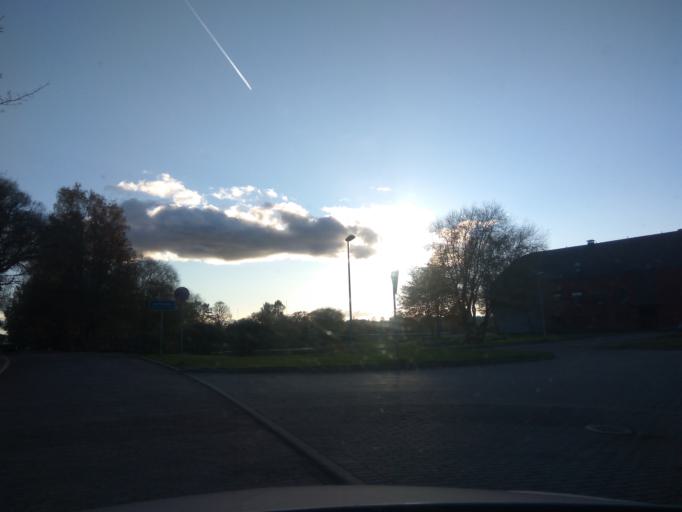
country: LV
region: Kuldigas Rajons
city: Kuldiga
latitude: 56.9655
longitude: 21.9665
